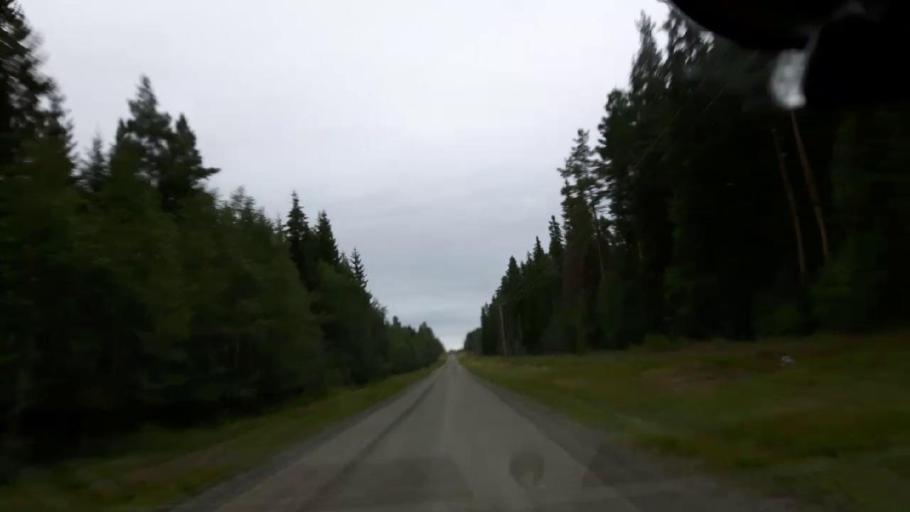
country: SE
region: Vaesternorrland
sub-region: Ange Kommun
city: Fransta
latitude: 62.8020
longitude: 16.0233
